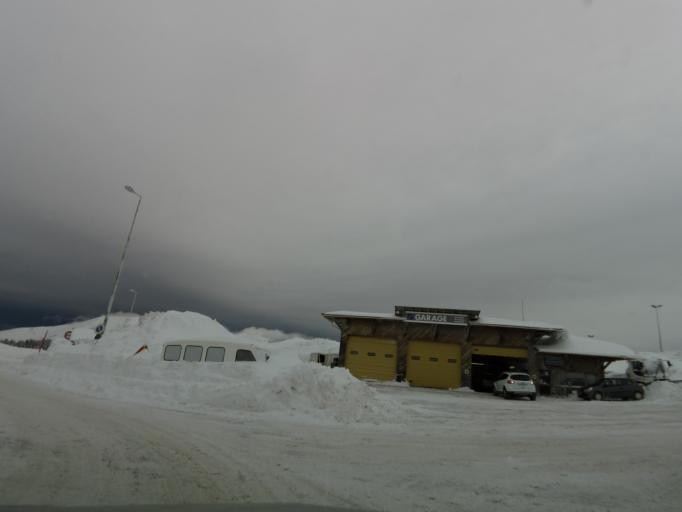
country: FR
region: Rhone-Alpes
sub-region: Departement de la Haute-Savoie
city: Morzine
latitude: 46.1962
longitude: 6.7677
